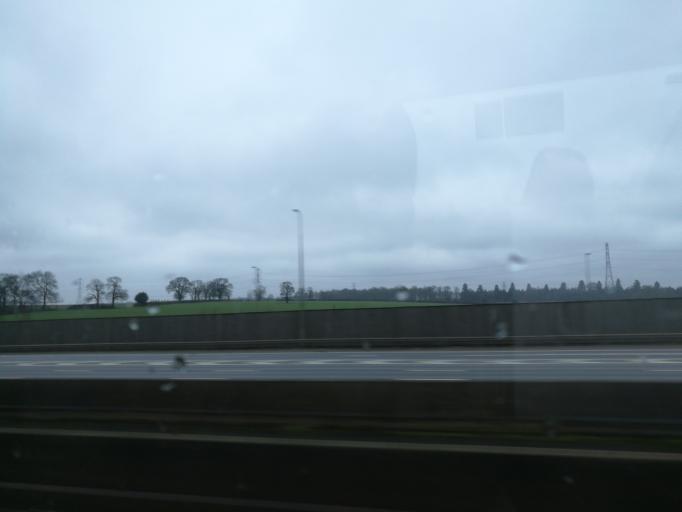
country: GB
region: England
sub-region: Hertfordshire
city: Abbots Langley
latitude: 51.7481
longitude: -0.4077
